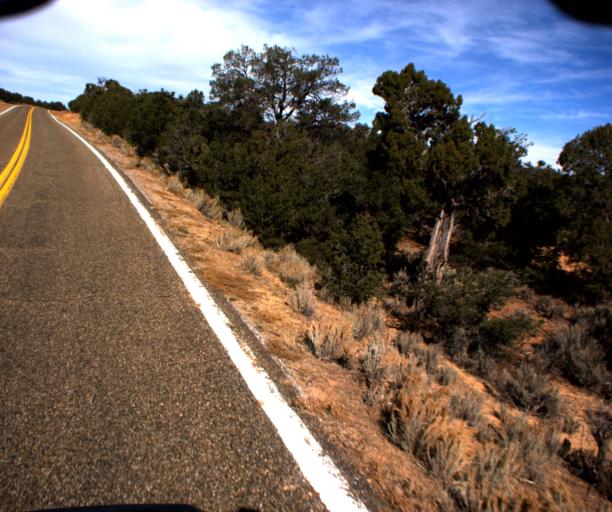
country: US
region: Arizona
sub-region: Navajo County
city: Kayenta
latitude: 36.5871
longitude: -110.4919
